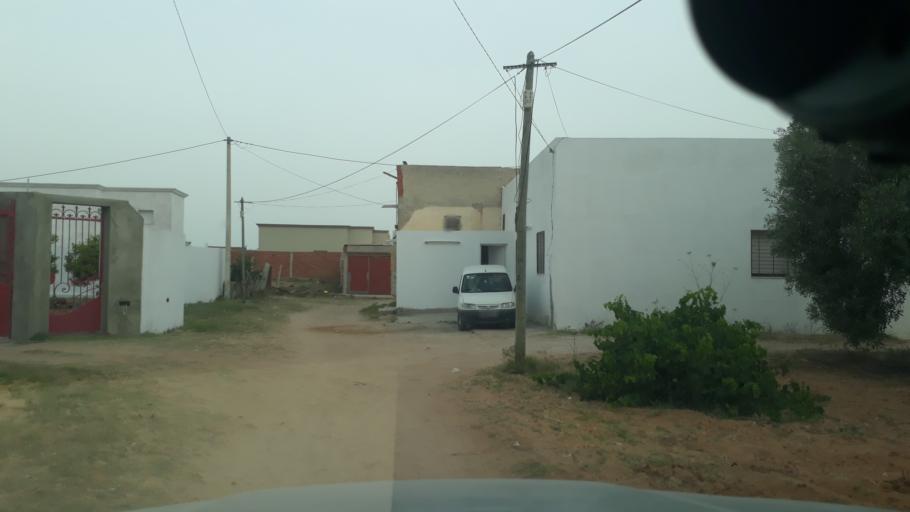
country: TN
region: Safaqis
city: Al Qarmadah
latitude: 34.7824
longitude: 10.7691
